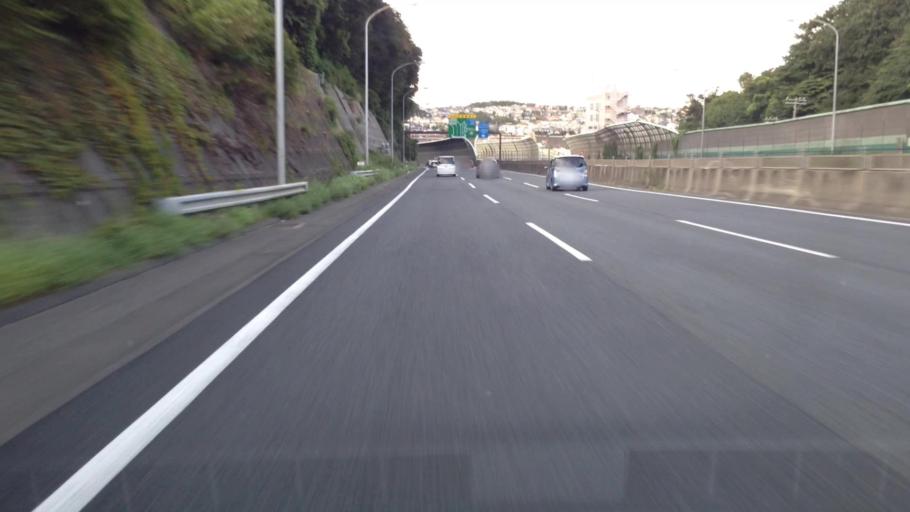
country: JP
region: Kanagawa
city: Yokohama
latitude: 35.4590
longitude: 139.5858
